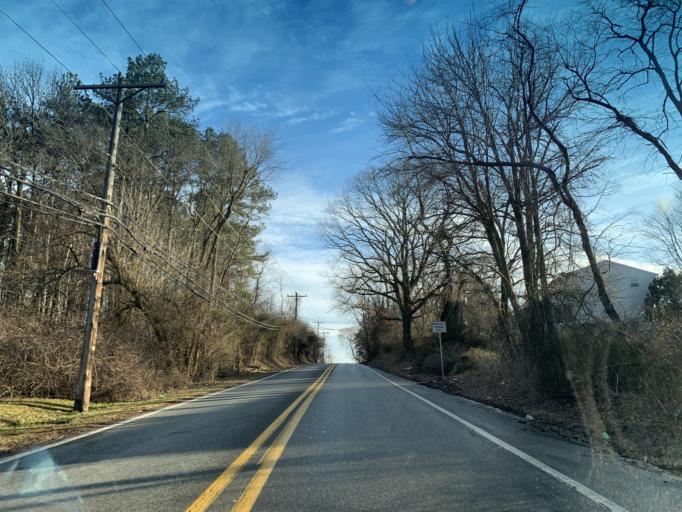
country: US
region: Delaware
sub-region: New Castle County
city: Bear
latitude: 39.6702
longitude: -75.6587
